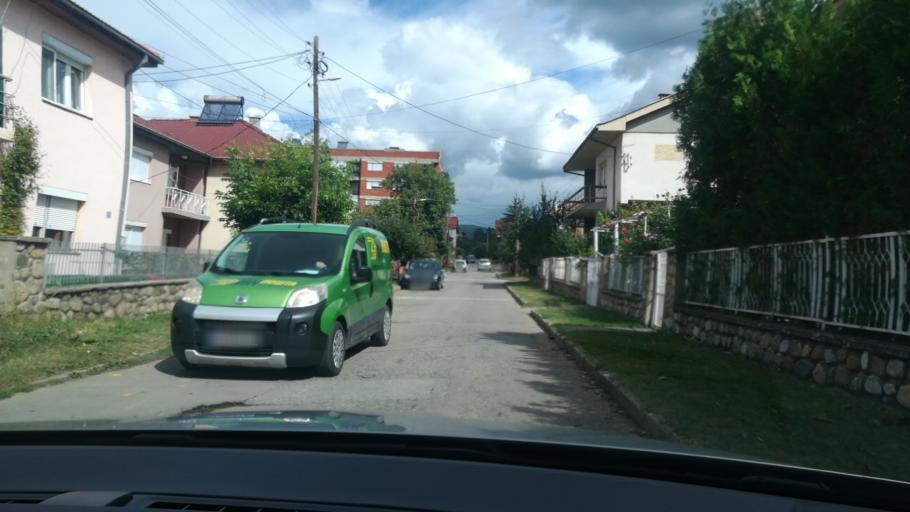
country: MK
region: Delcevo
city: Delcevo
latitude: 41.9624
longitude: 22.7781
